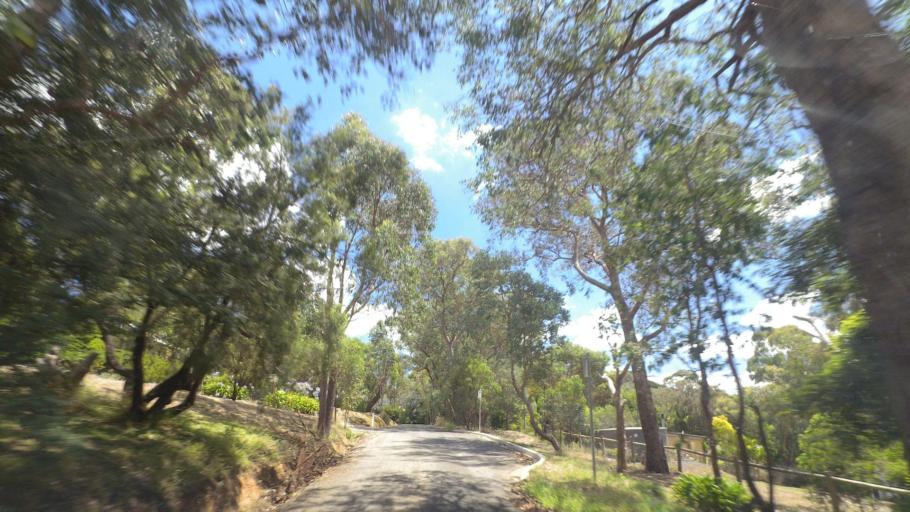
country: AU
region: Victoria
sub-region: Yarra Ranges
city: Chirnside Park
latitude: -37.7326
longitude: 145.2766
